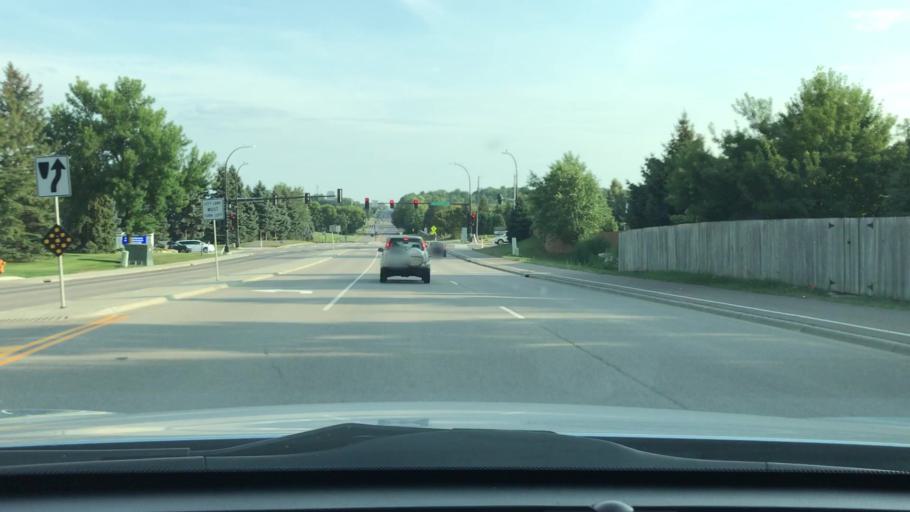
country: US
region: Minnesota
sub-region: Hennepin County
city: Plymouth
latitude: 45.0332
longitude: -93.4818
